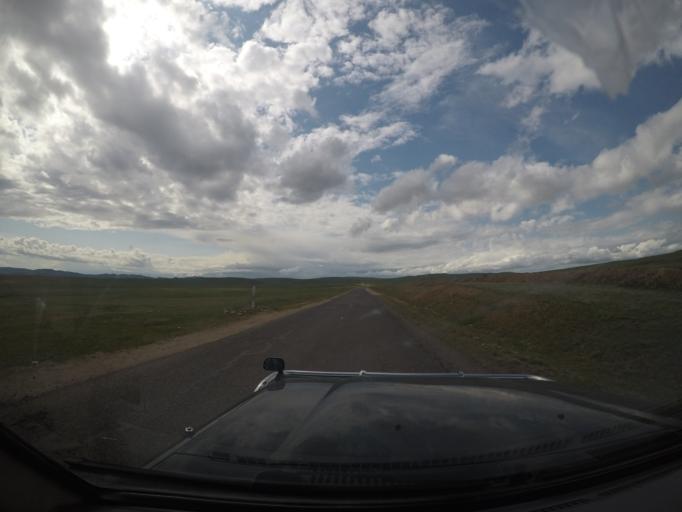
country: MN
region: Hentiy
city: Modot
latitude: 47.5547
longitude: 109.3512
